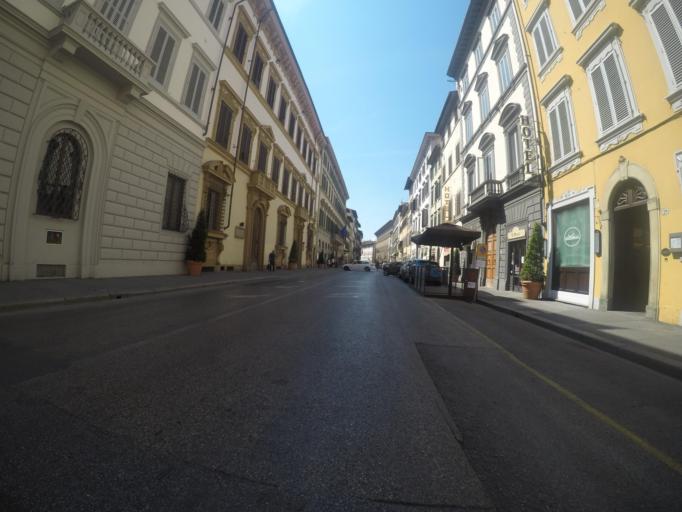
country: IT
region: Tuscany
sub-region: Province of Florence
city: Florence
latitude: 43.7767
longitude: 11.2570
